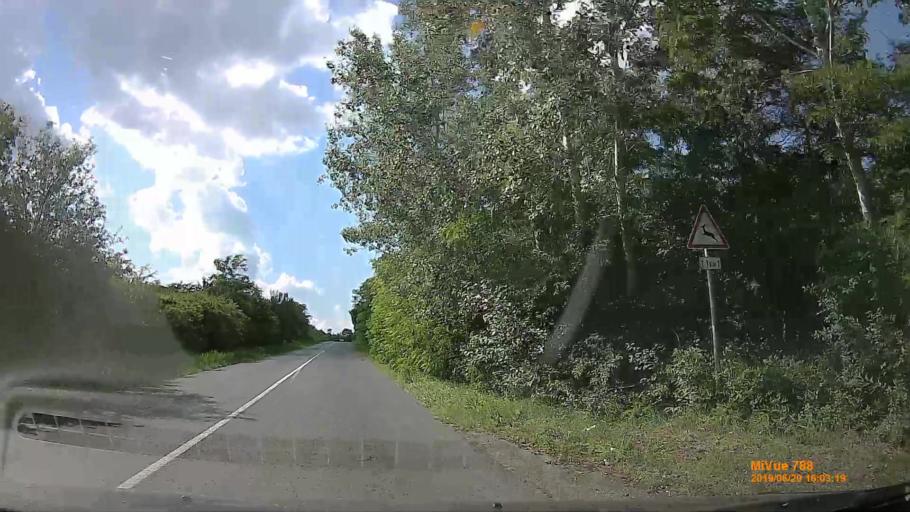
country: HU
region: Baranya
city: Pellerd
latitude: 46.0626
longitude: 18.1163
